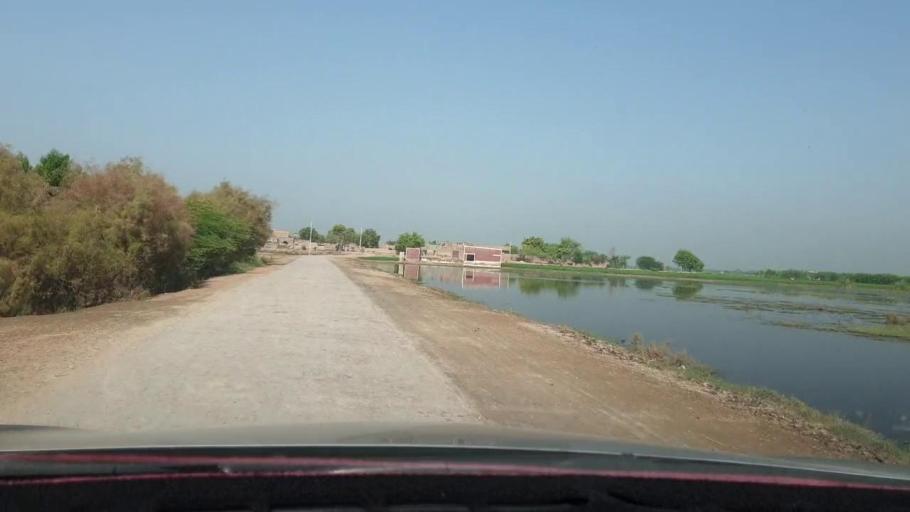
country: PK
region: Sindh
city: Kambar
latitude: 27.5993
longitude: 67.9779
